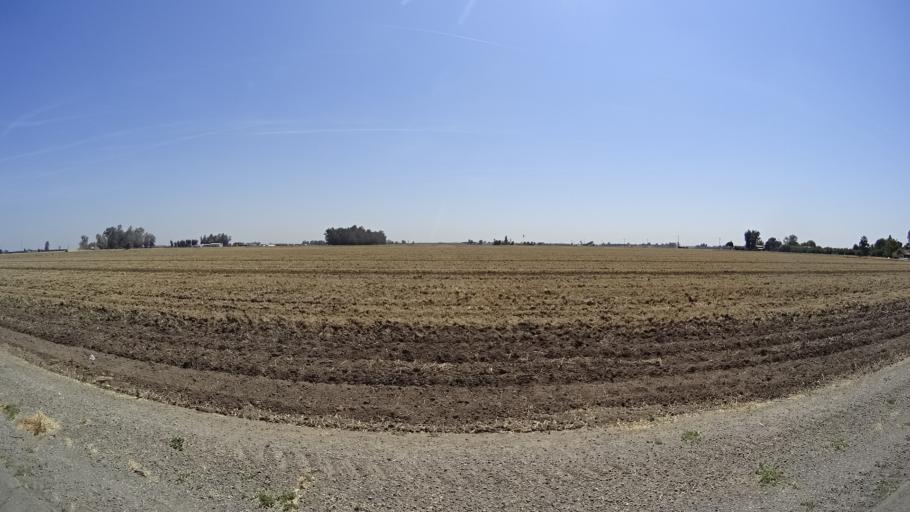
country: US
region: California
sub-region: Fresno County
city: Riverdale
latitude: 36.4039
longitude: -119.8515
